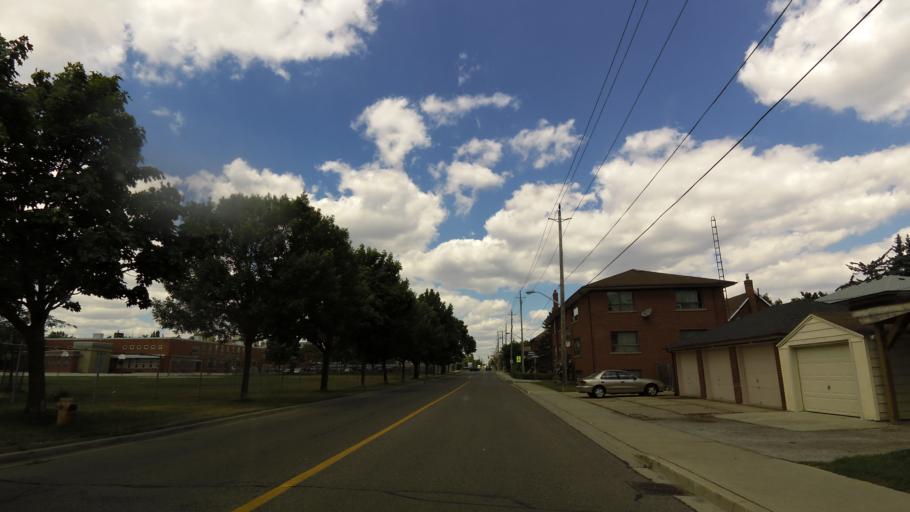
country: CA
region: Ontario
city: Etobicoke
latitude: 43.6035
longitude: -79.4984
